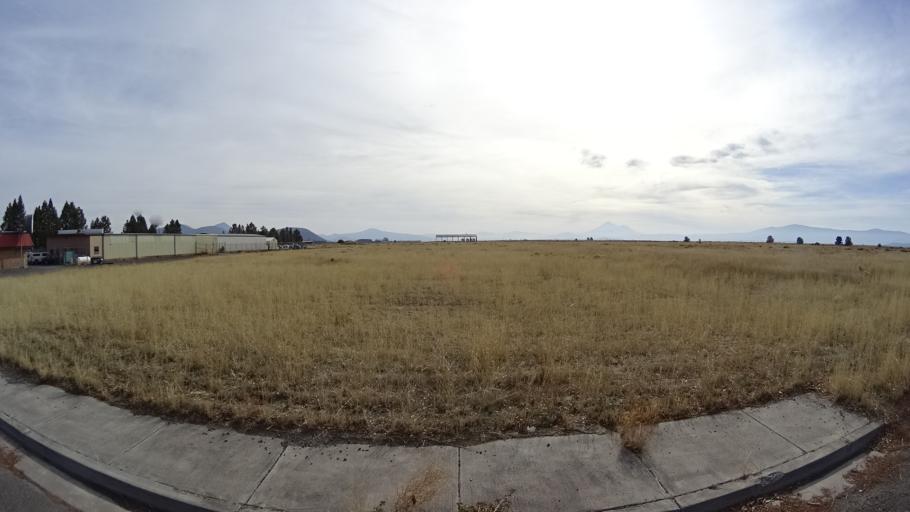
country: US
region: Oregon
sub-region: Klamath County
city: Klamath Falls
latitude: 41.9641
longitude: -121.9272
